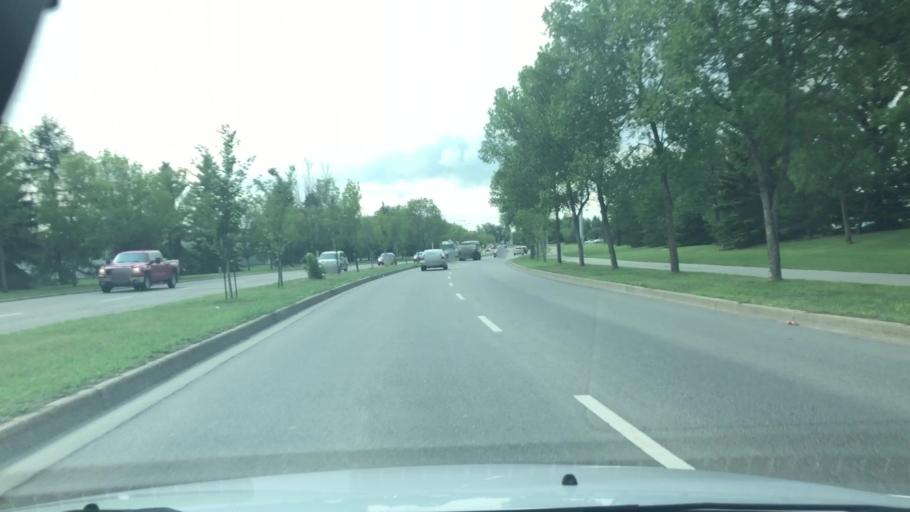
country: CA
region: Alberta
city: Edmonton
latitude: 53.6148
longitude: -113.5237
